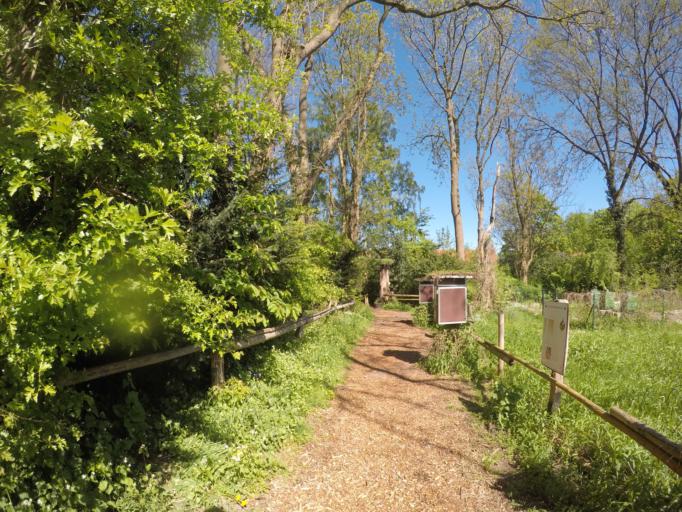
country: DE
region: Hamburg
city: Sasel
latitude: 53.6302
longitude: 10.1092
